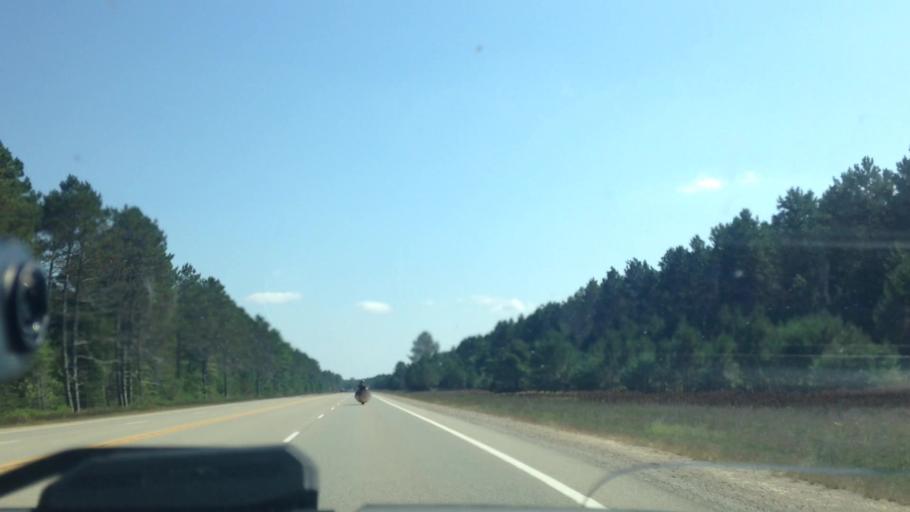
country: US
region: Michigan
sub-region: Alger County
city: Munising
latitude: 46.3582
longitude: -86.5164
